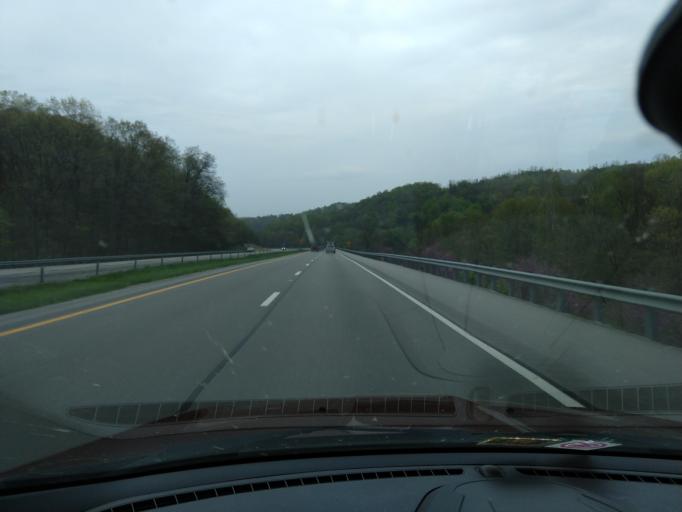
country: US
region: West Virginia
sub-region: Harrison County
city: Stonewood
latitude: 39.1414
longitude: -80.3669
